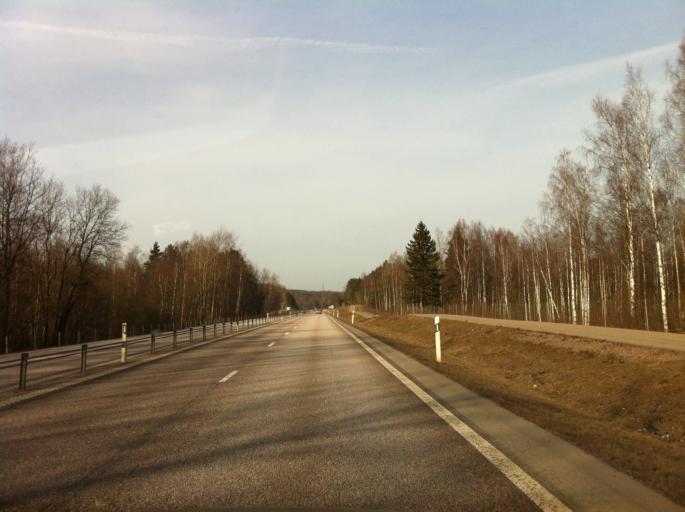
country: SE
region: Vaestra Goetaland
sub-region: Skovde Kommun
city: Stopen
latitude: 58.4374
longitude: 13.8576
